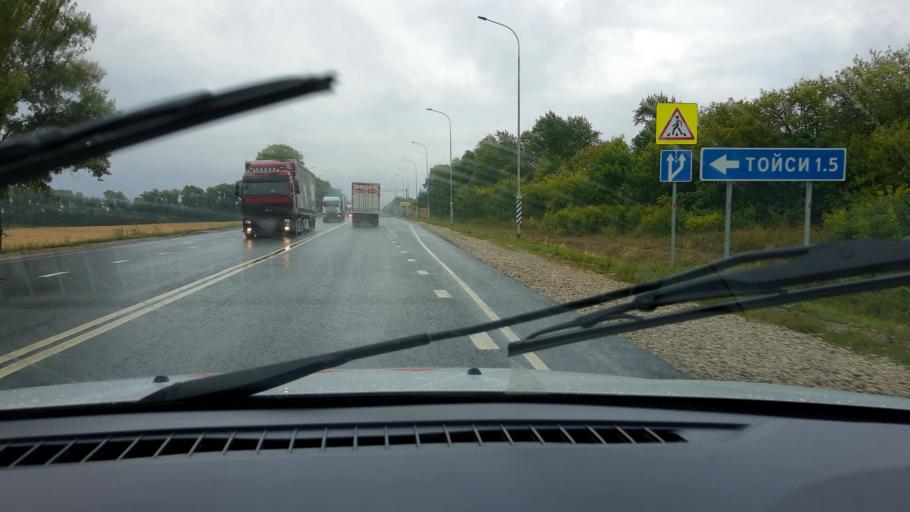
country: RU
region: Chuvashia
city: Tsivil'sk
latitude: 55.7900
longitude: 47.6883
